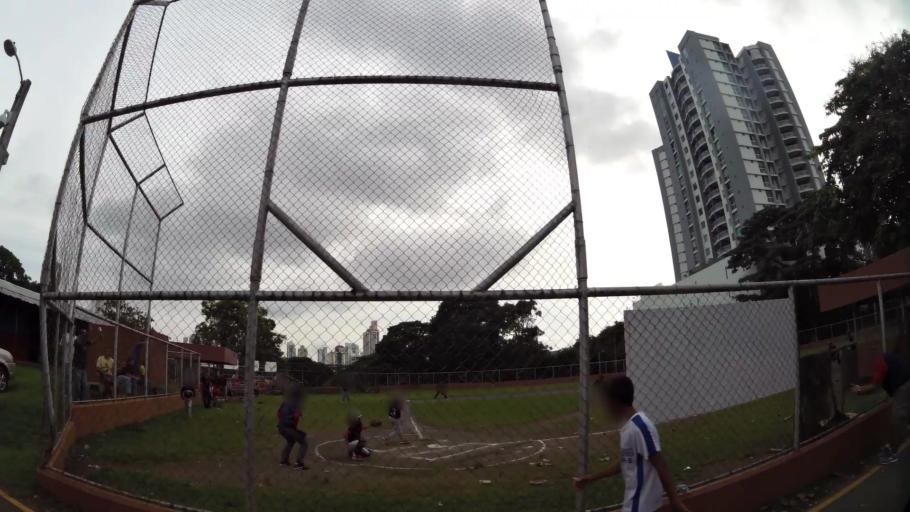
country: PA
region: Panama
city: Panama
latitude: 9.0007
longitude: -79.5096
